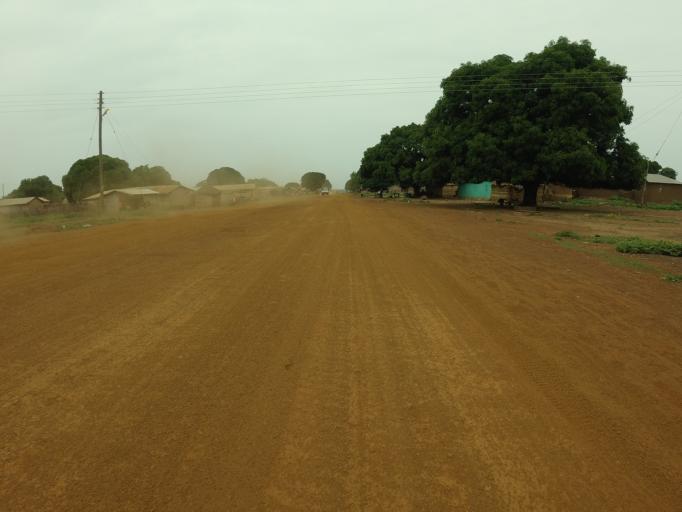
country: GH
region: Northern
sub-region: Yendi
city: Yendi
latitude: 9.2818
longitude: 0.0180
